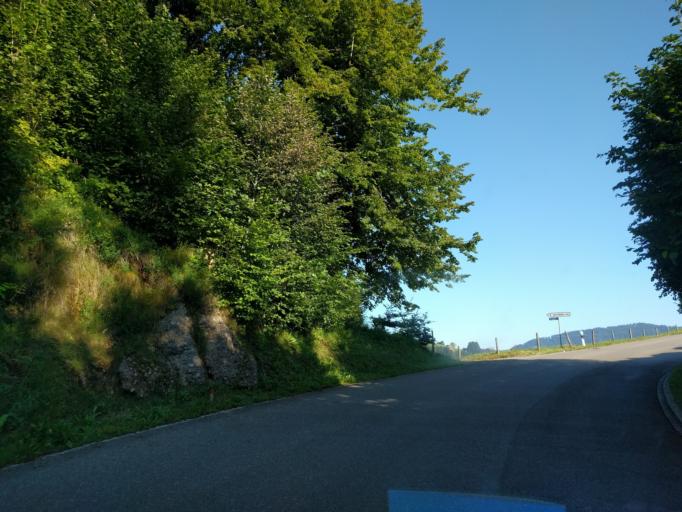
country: CH
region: Saint Gallen
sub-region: Wahlkreis Toggenburg
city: Sankt Peterzell
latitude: 47.2993
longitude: 9.1899
